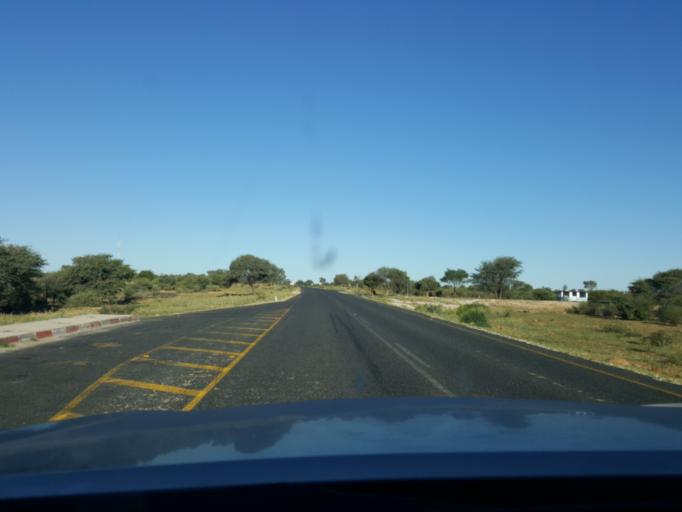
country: BW
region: Southern
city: Khakhea
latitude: -24.2294
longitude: 23.2450
